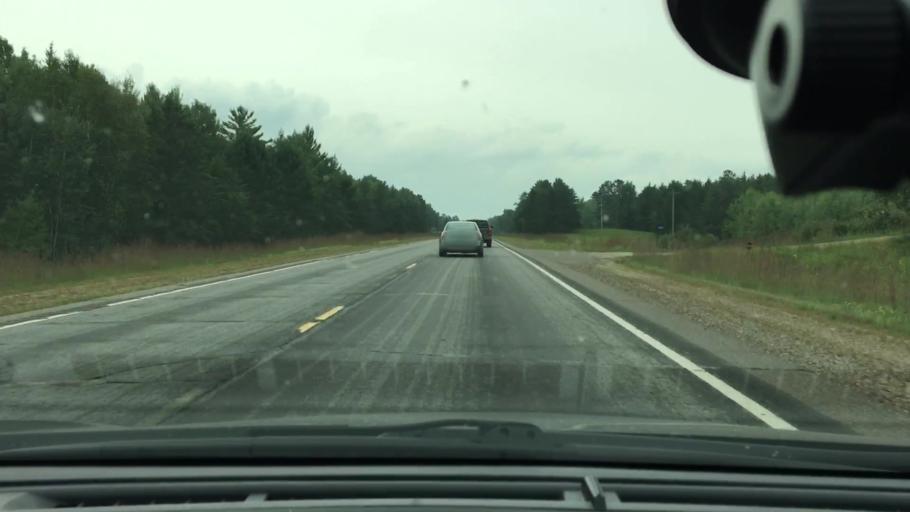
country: US
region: Minnesota
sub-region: Crow Wing County
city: Cross Lake
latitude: 46.6852
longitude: -93.9537
